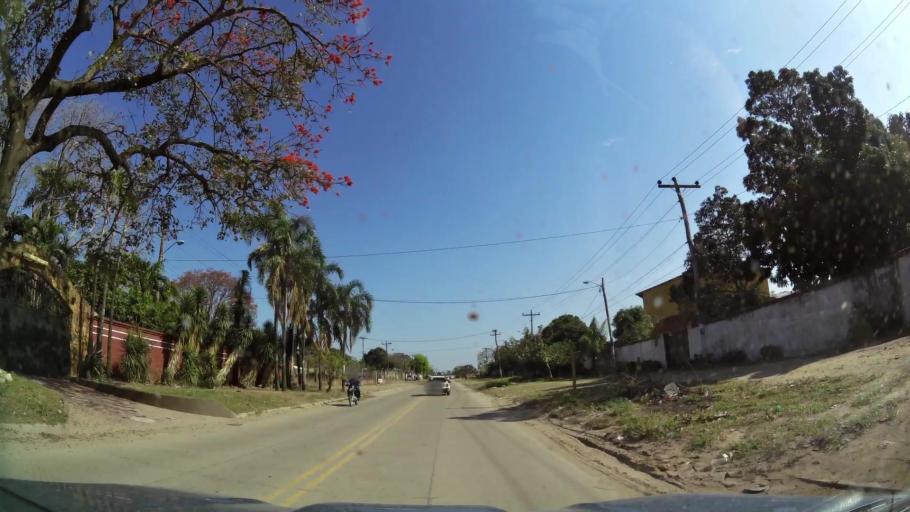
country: BO
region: Santa Cruz
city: Santa Cruz de la Sierra
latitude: -17.7630
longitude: -63.1114
